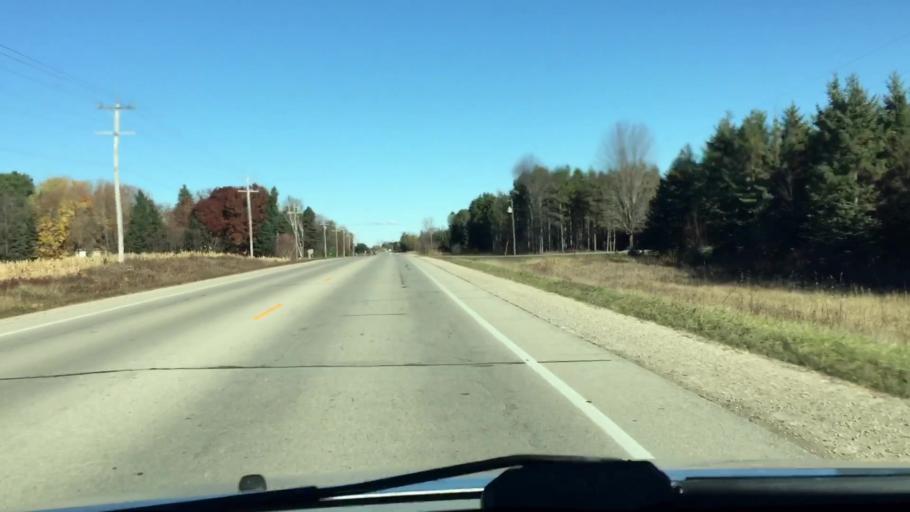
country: US
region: Wisconsin
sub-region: Brown County
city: Pulaski
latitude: 44.7033
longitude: -88.2439
